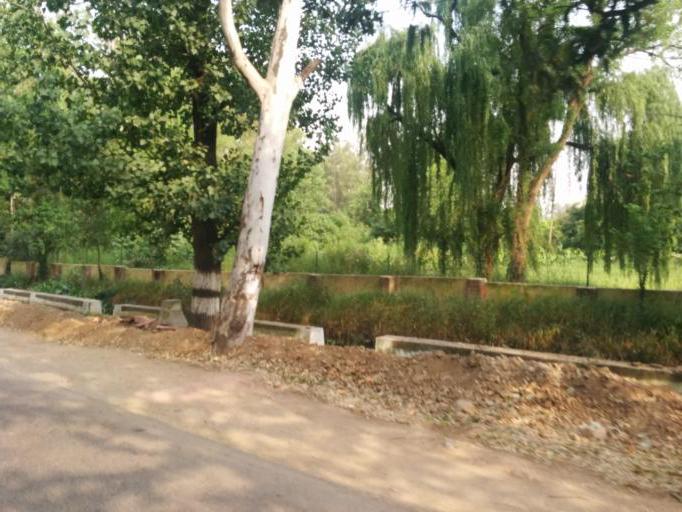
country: IN
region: Punjab
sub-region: Gurdaspur
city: Dharkalan
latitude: 32.2835
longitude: 75.8562
